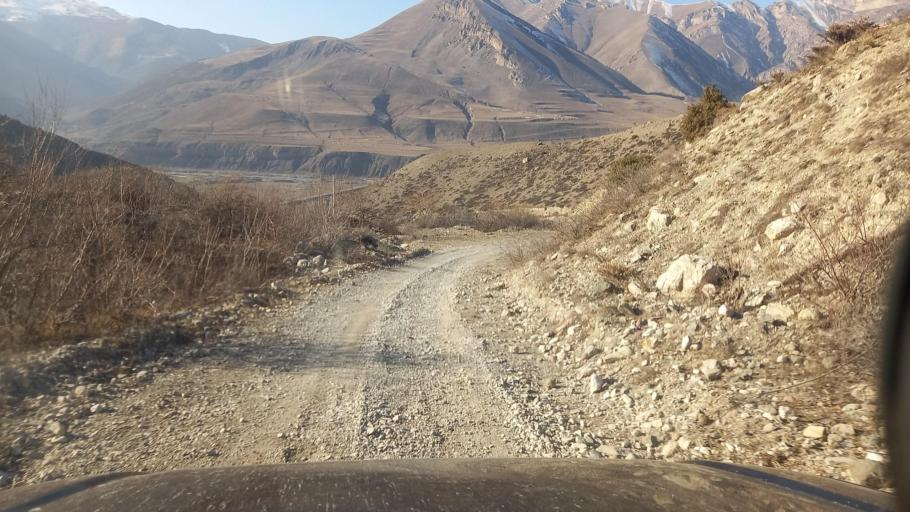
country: RU
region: Ingushetiya
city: Dzhayrakh
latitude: 42.8455
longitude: 44.6550
